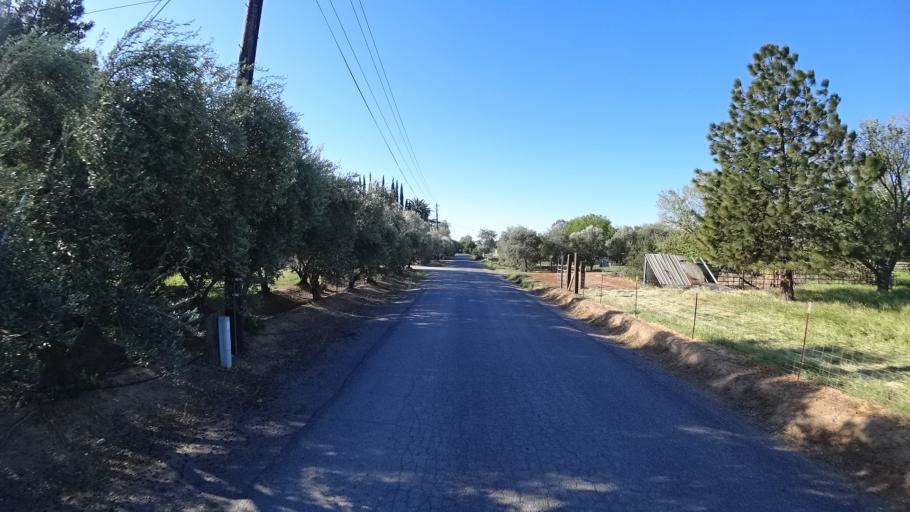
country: US
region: California
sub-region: Glenn County
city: Orland
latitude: 39.7240
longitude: -122.1878
